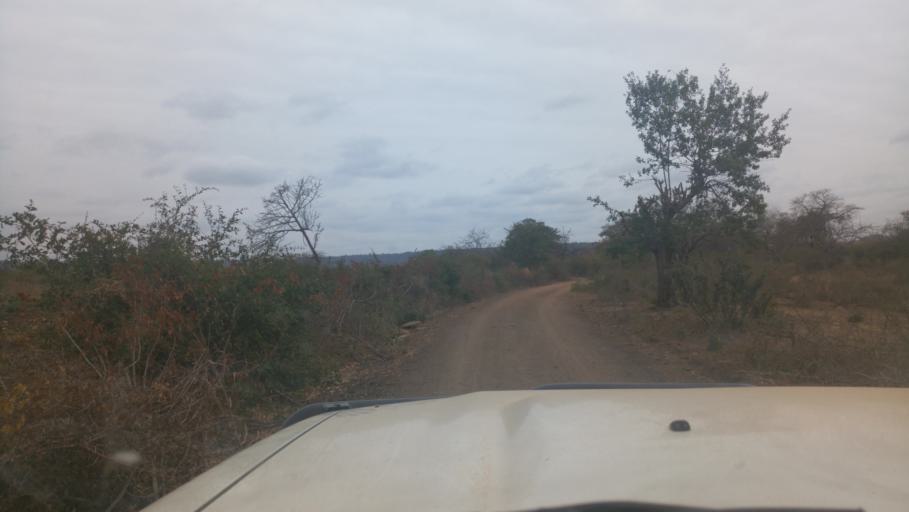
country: KE
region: Makueni
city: Makueni
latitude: -2.0265
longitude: 38.1001
